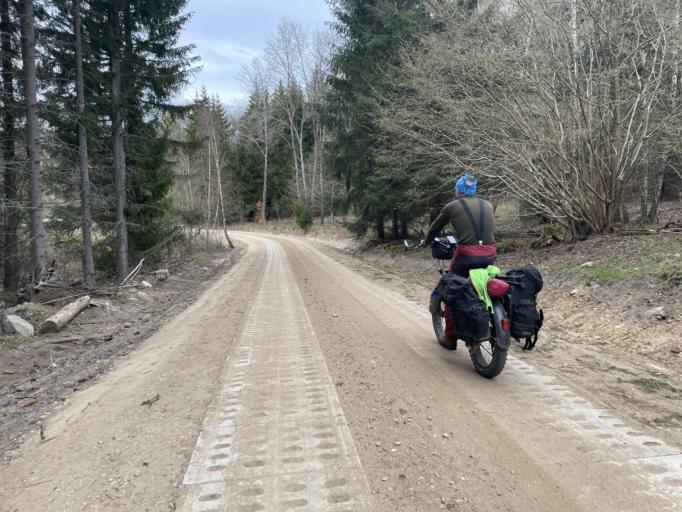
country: PL
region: West Pomeranian Voivodeship
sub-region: Powiat szczecinecki
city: Bialy Bor
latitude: 53.9073
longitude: 16.7225
